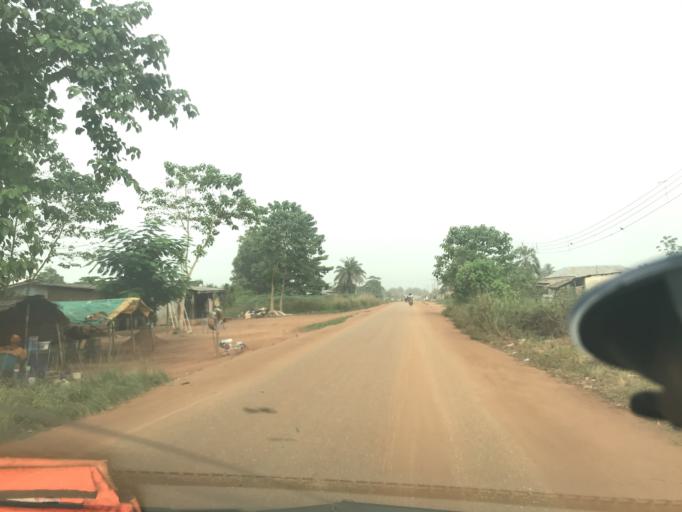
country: NG
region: Ogun
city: Ado Odo
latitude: 6.5758
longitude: 2.9375
